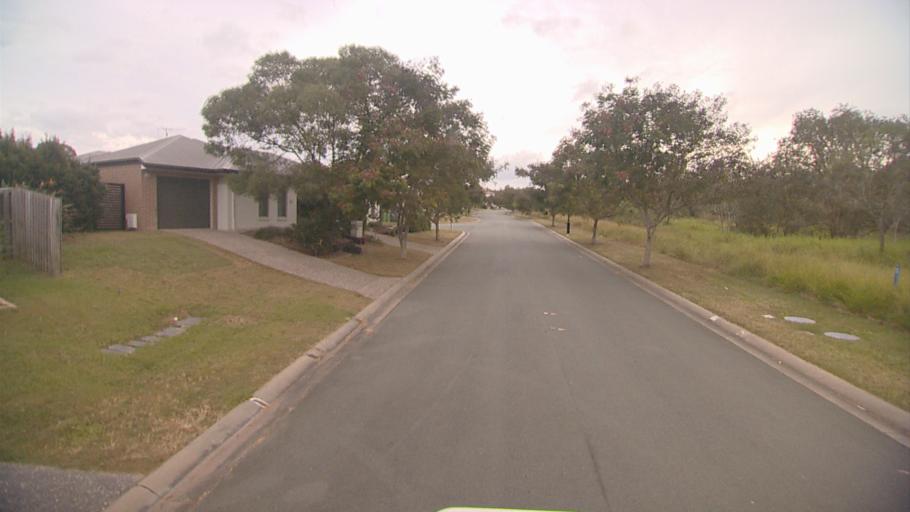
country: AU
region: Queensland
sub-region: Logan
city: Windaroo
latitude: -27.7185
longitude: 153.1713
